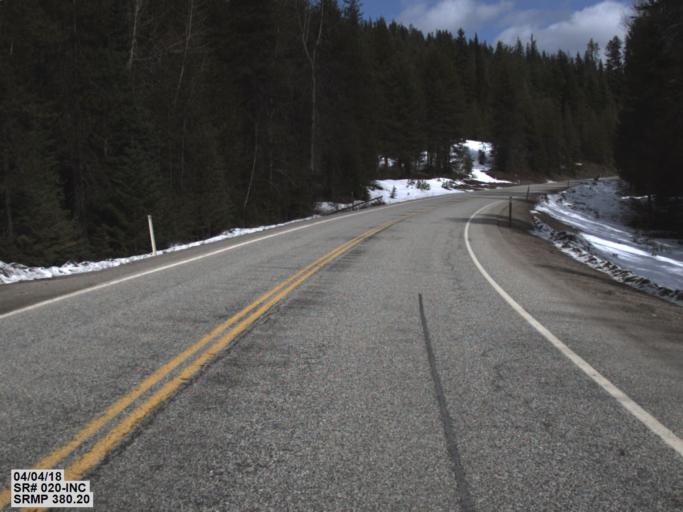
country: US
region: Washington
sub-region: Stevens County
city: Colville
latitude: 48.6266
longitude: -117.5454
